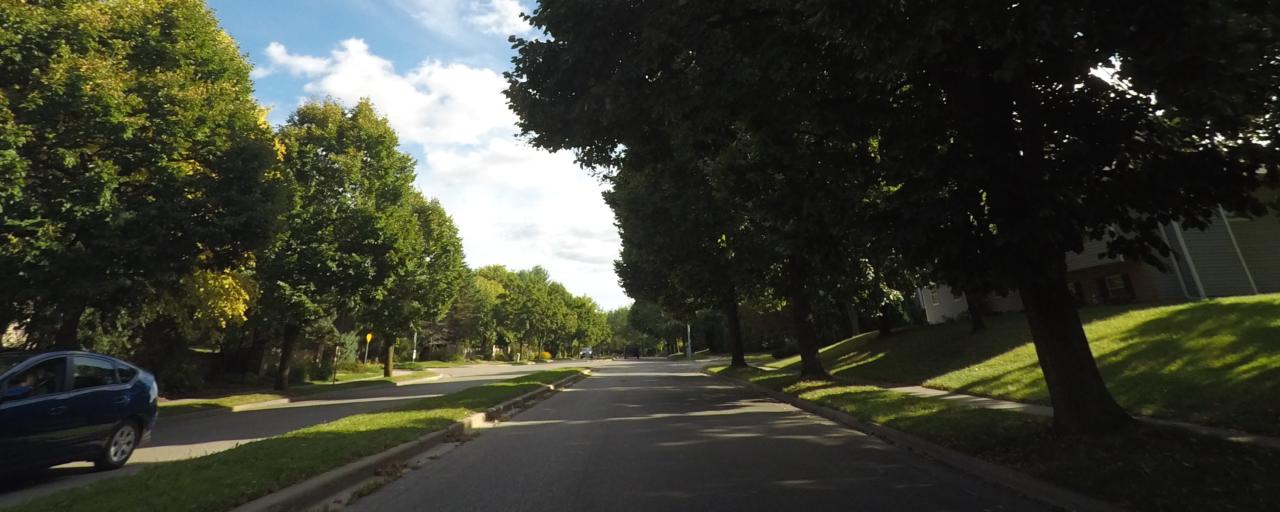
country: US
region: Wisconsin
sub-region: Dane County
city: Middleton
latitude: 43.0679
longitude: -89.5176
